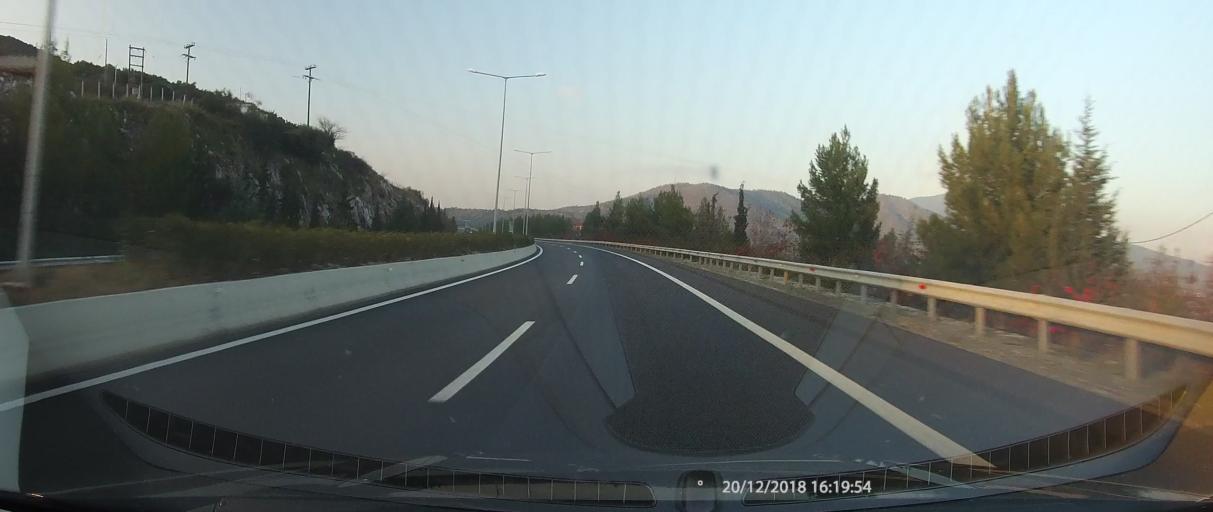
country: GR
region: Thessaly
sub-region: Nomos Magnisias
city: Pteleos
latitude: 39.0187
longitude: 22.9159
